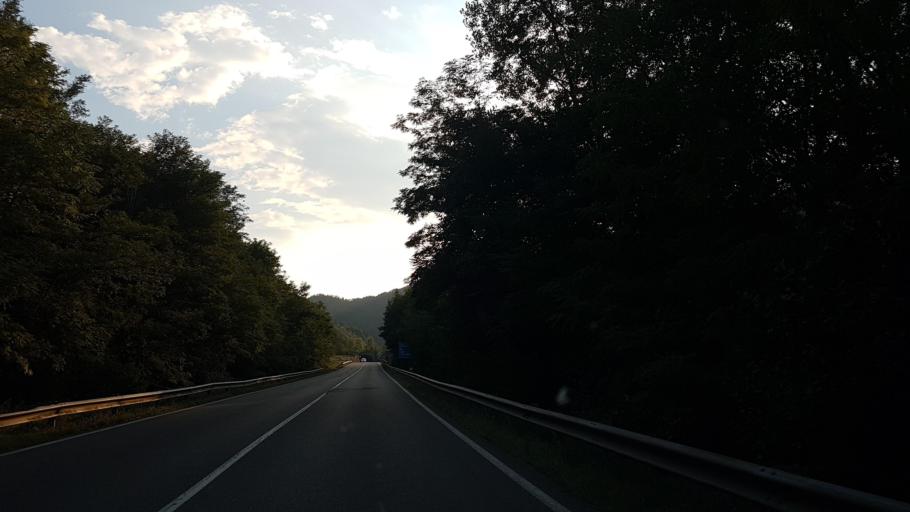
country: IT
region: Emilia-Romagna
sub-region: Provincia di Parma
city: Stazione Valmozzola
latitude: 44.5314
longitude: 9.8726
